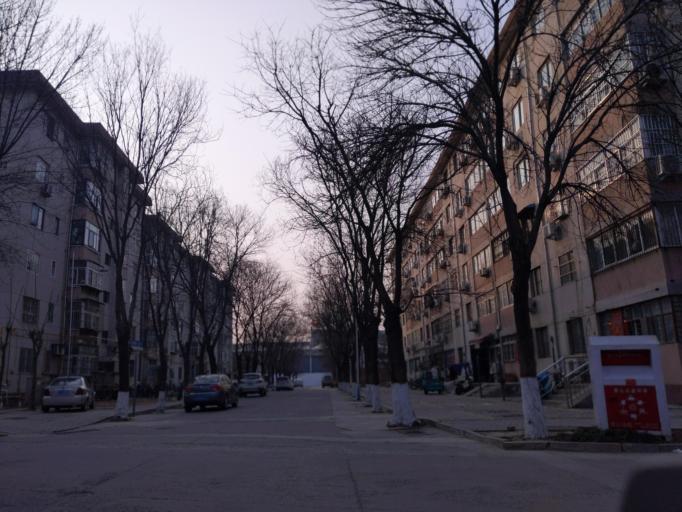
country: CN
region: Henan Sheng
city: Zhongyuanlu
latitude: 35.7821
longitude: 115.0575
